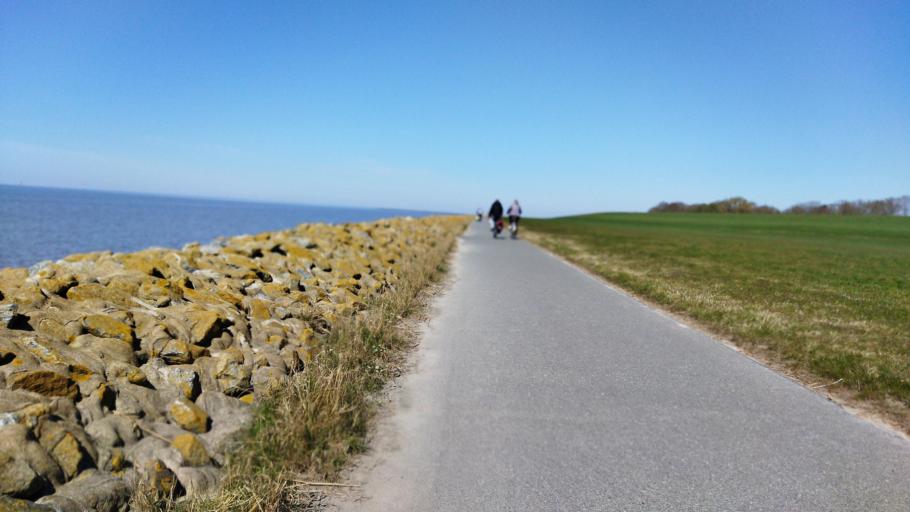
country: DE
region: Lower Saxony
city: Wremen
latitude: 53.6239
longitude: 8.5085
